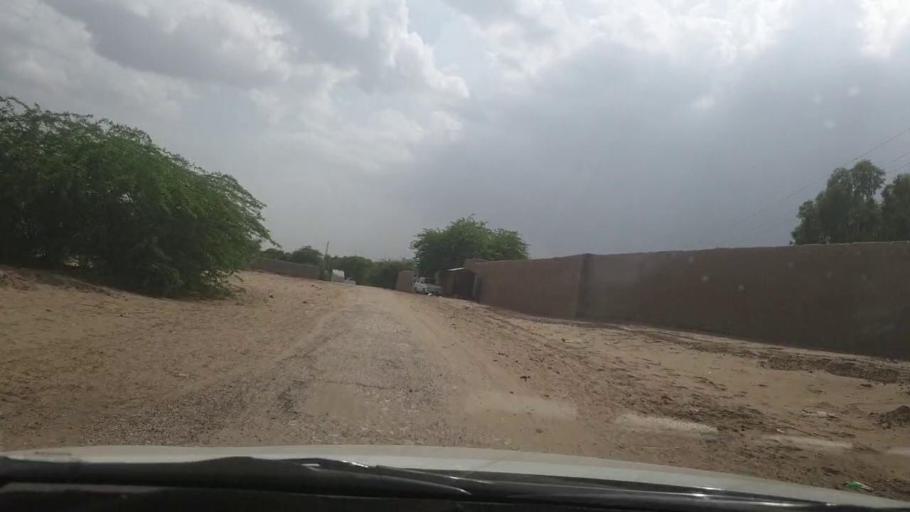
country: PK
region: Sindh
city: Kot Diji
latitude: 27.3384
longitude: 69.0144
